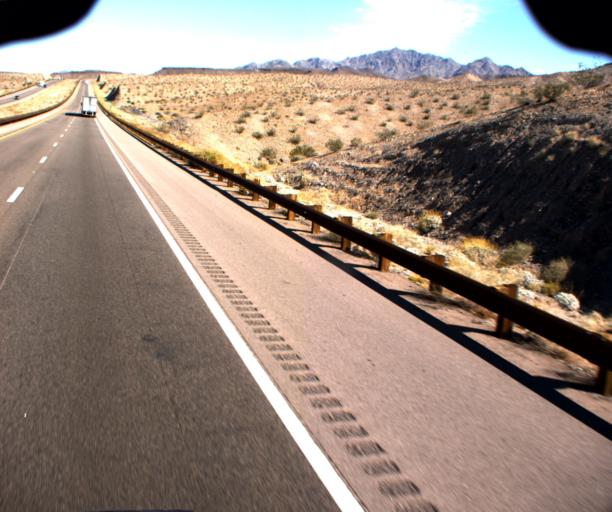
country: US
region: Nevada
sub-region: Clark County
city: Boulder City
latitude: 35.9184
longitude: -114.6304
